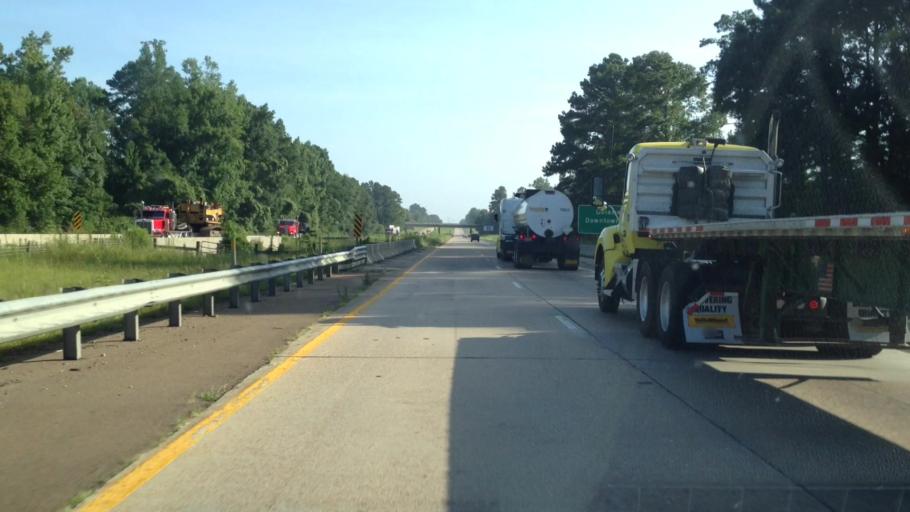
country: US
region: Mississippi
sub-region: Pike County
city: McComb
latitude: 31.2324
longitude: -90.4816
